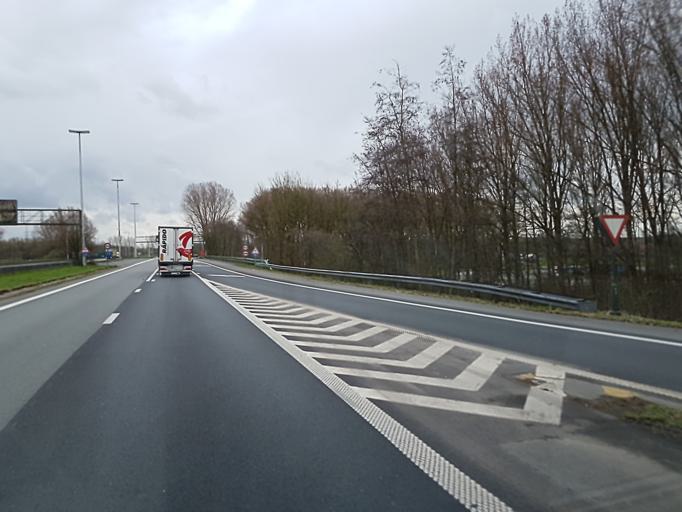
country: BE
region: Wallonia
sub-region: Province du Hainaut
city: Rumes
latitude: 50.6153
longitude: 3.3235
